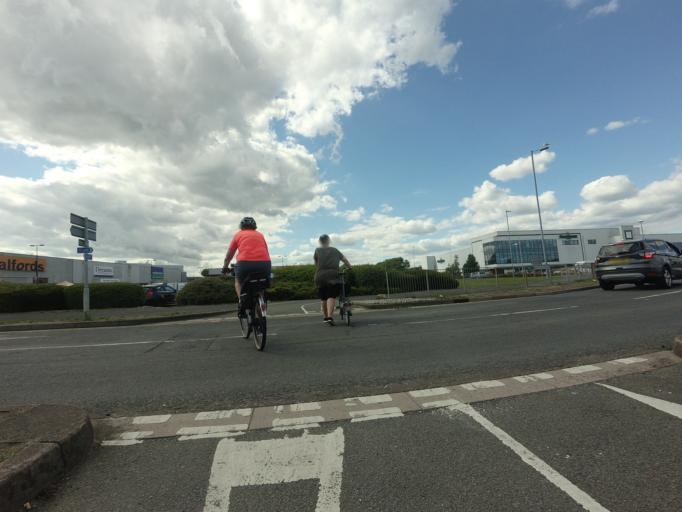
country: GB
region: England
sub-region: East Sussex
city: Eastbourne
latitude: 50.7953
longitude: 0.2853
